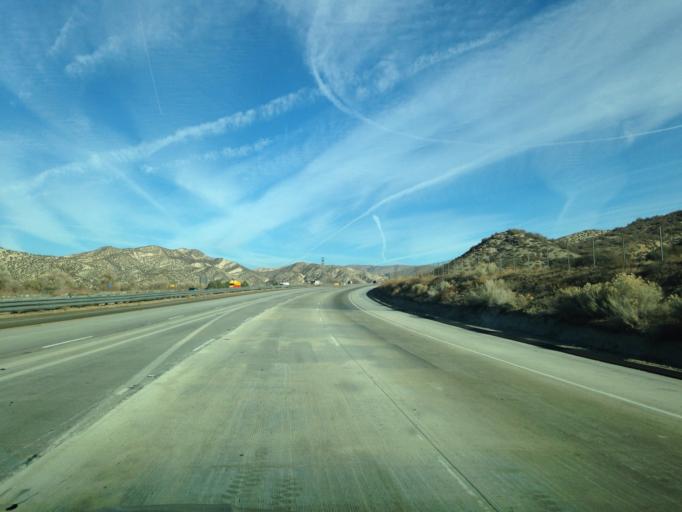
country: US
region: California
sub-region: Kern County
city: Lebec
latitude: 34.7119
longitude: -118.7977
